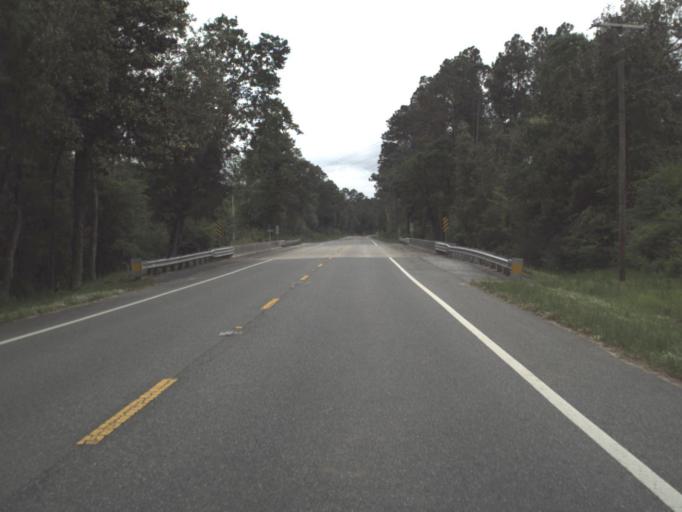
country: US
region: Florida
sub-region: Santa Rosa County
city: Point Baker
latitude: 30.8030
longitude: -87.0424
